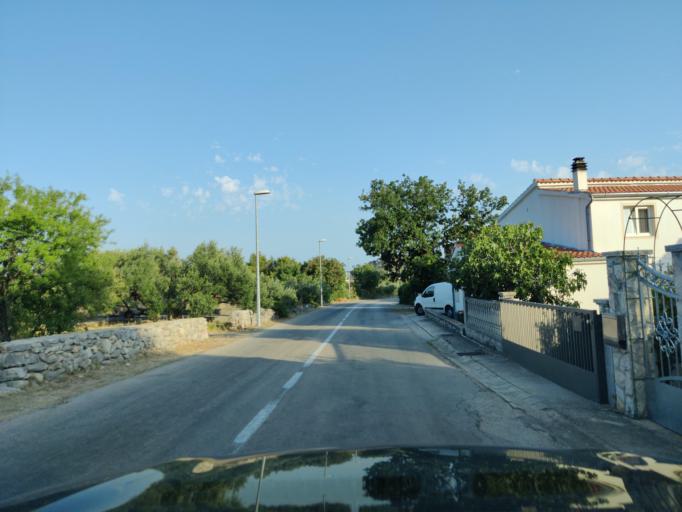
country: HR
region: Sibensko-Kniniska
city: Tribunj
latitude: 43.7631
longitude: 15.7385
